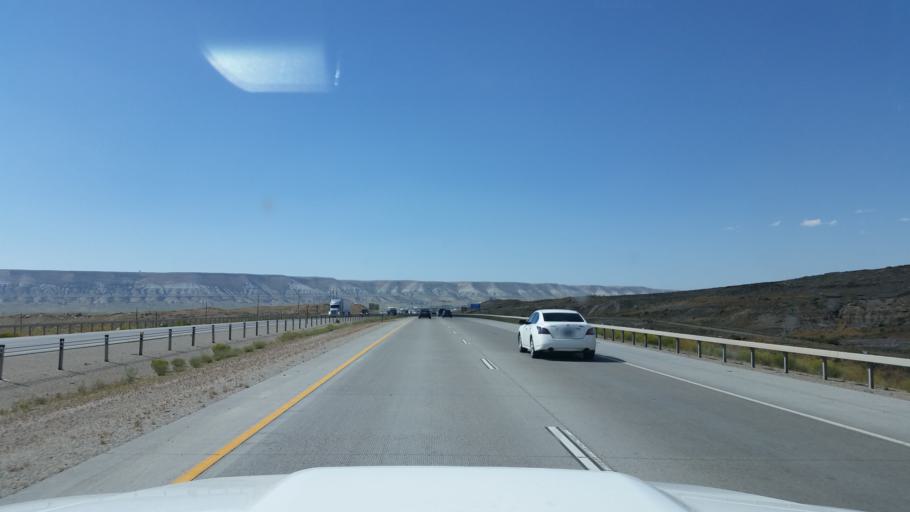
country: US
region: Wyoming
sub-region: Sweetwater County
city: Rock Springs
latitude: 41.6057
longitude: -109.2076
